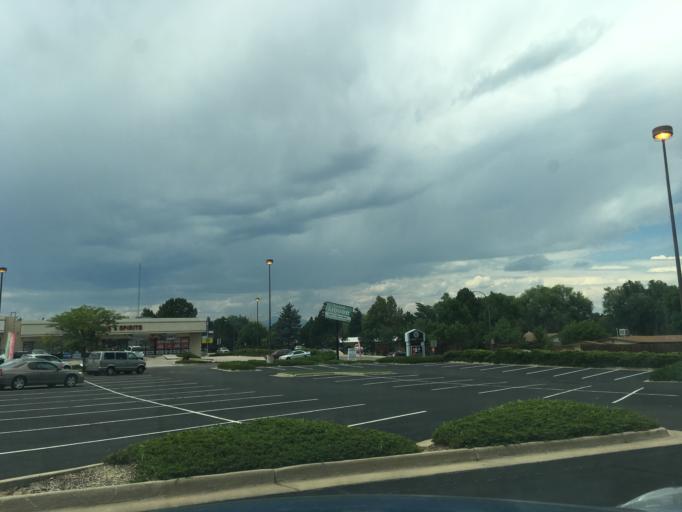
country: US
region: Colorado
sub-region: Jefferson County
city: Lakewood
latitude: 39.6818
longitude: -105.0541
